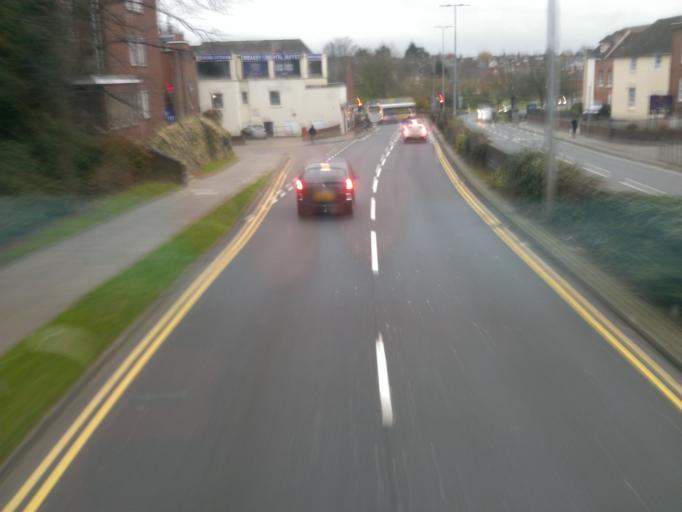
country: GB
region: England
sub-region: Essex
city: Colchester
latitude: 51.8886
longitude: 0.8938
